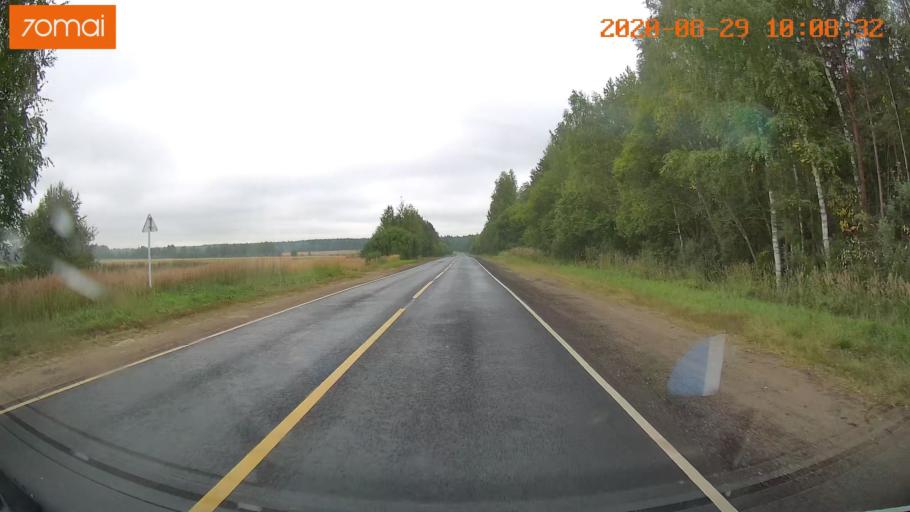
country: RU
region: Ivanovo
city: Kuznechikha
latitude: 57.3757
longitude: 42.5927
